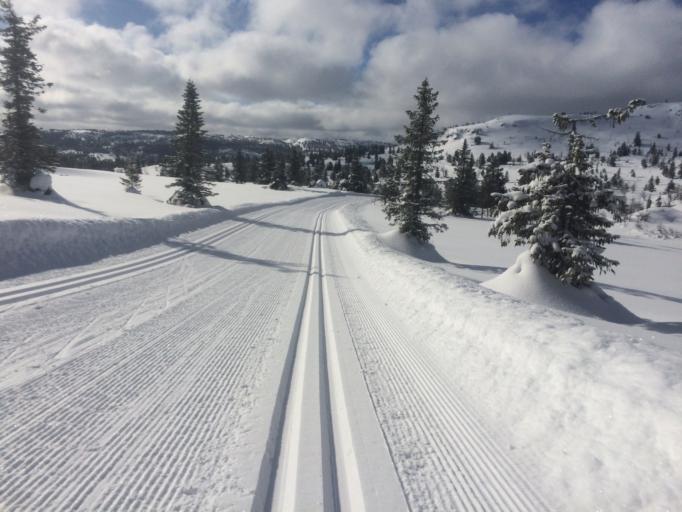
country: NO
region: Oppland
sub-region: Ringebu
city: Ringebu
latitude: 61.3569
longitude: 10.0587
